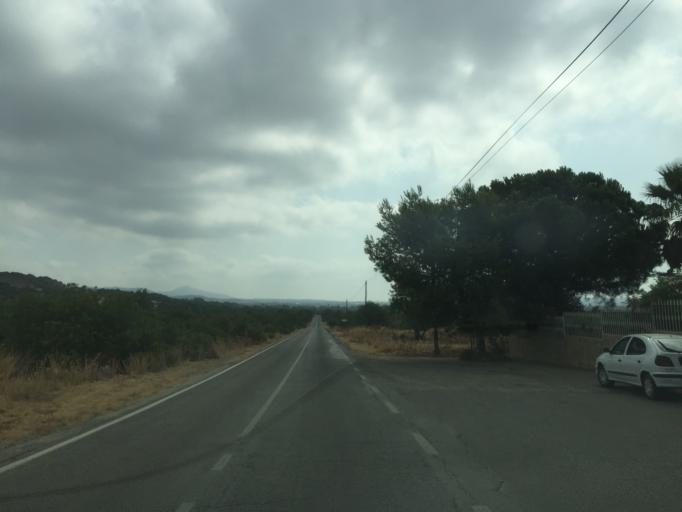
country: PT
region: Faro
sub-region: Faro
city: Santa Barbara de Nexe
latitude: 37.0911
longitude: -7.9371
